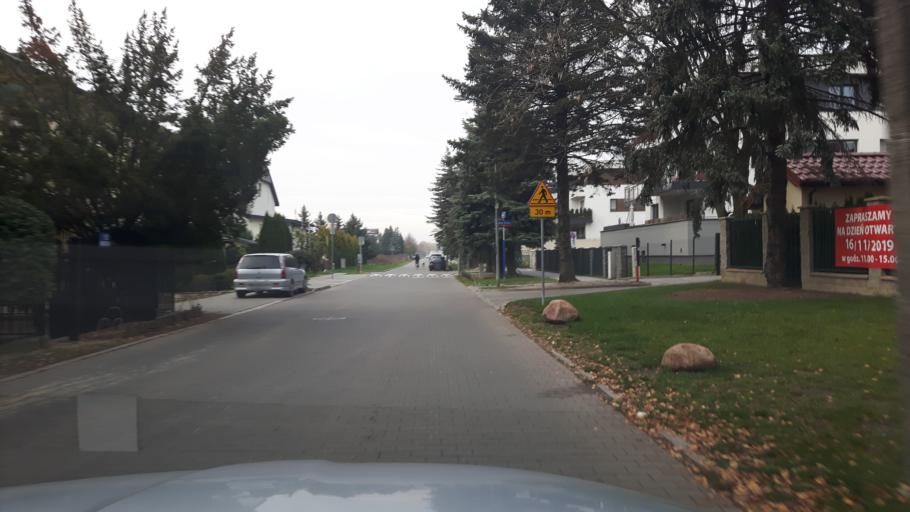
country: PL
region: Masovian Voivodeship
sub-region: Warszawa
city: Wilanow
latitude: 52.1721
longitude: 21.1132
